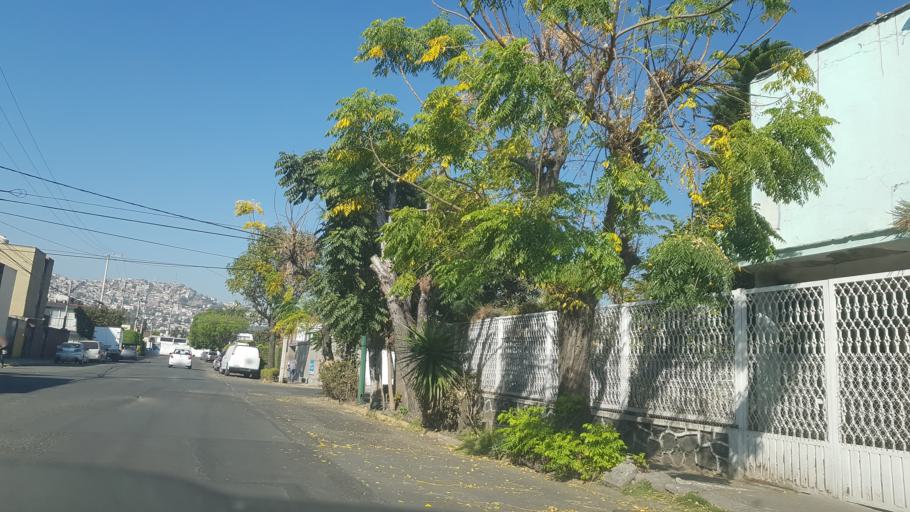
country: MX
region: Mexico
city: Naucalpan de Juarez
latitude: 19.4922
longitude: -99.2488
